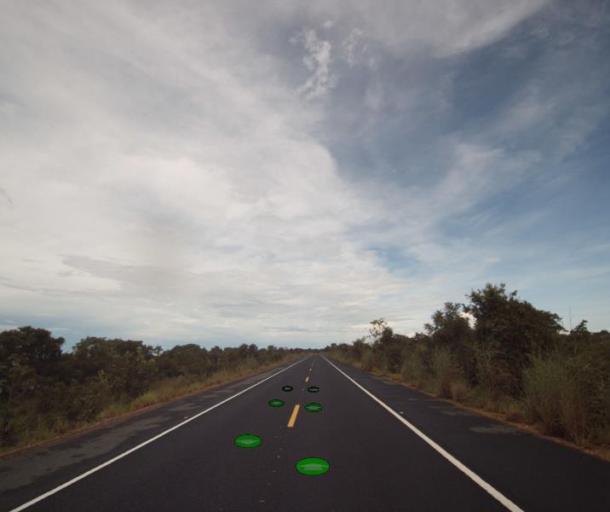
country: BR
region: Goias
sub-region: Sao Miguel Do Araguaia
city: Sao Miguel do Araguaia
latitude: -13.2381
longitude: -50.5485
